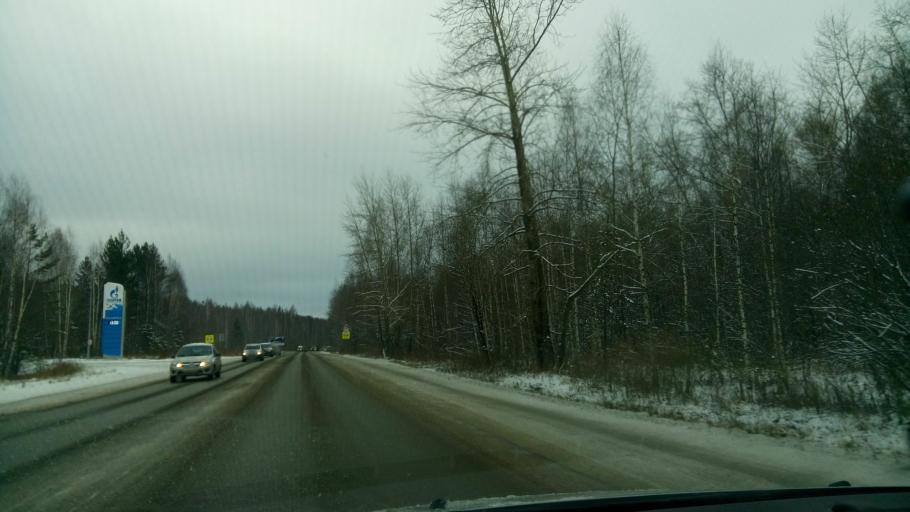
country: RU
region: Sverdlovsk
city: Polevskoy
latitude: 56.4668
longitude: 60.2254
